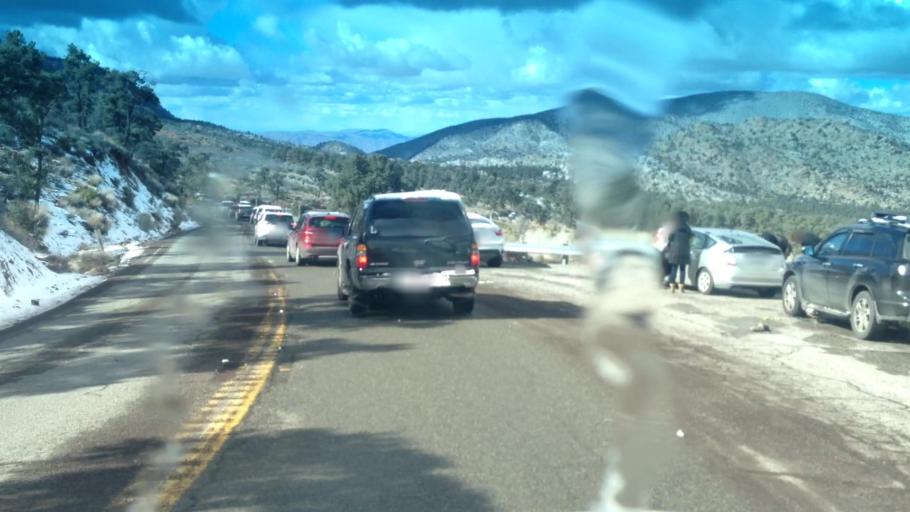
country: US
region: California
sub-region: San Bernardino County
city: Big Bear City
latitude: 34.3030
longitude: -116.8031
